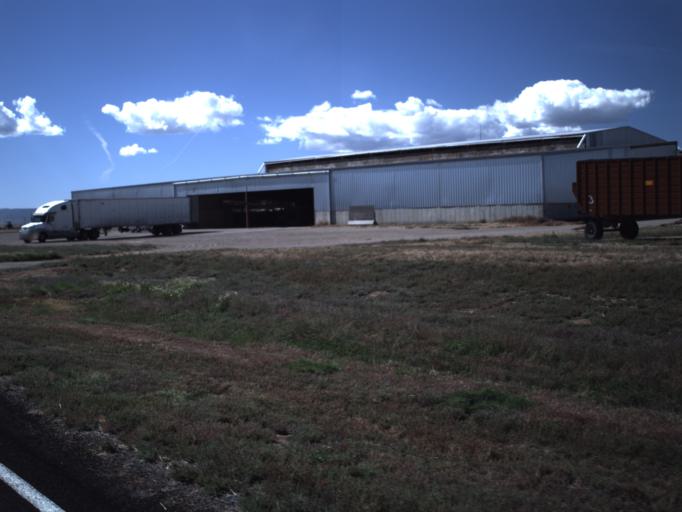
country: US
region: Utah
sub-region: Washington County
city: Enterprise
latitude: 37.6781
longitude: -113.6565
